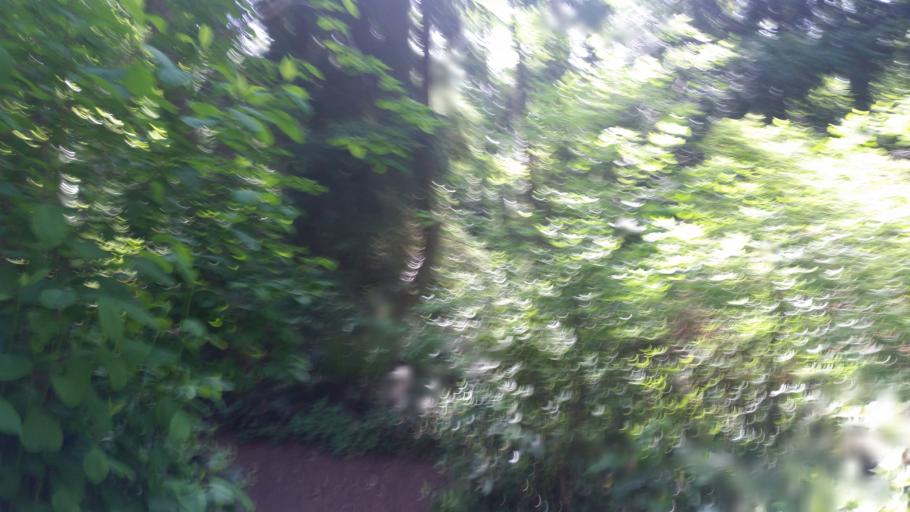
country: US
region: Washington
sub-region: Snohomish County
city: Esperance
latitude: 47.8077
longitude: -122.3578
